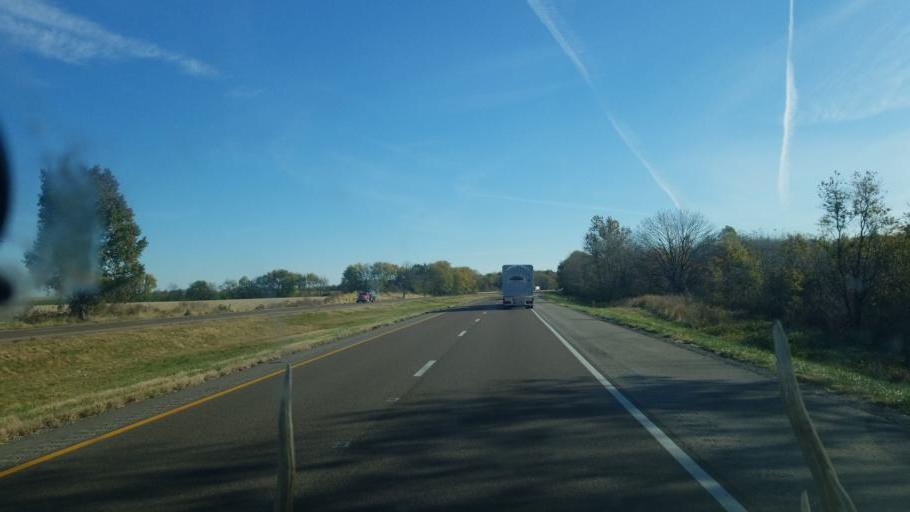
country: US
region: Illinois
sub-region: Madison County
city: Troy
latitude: 38.7599
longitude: -89.8340
